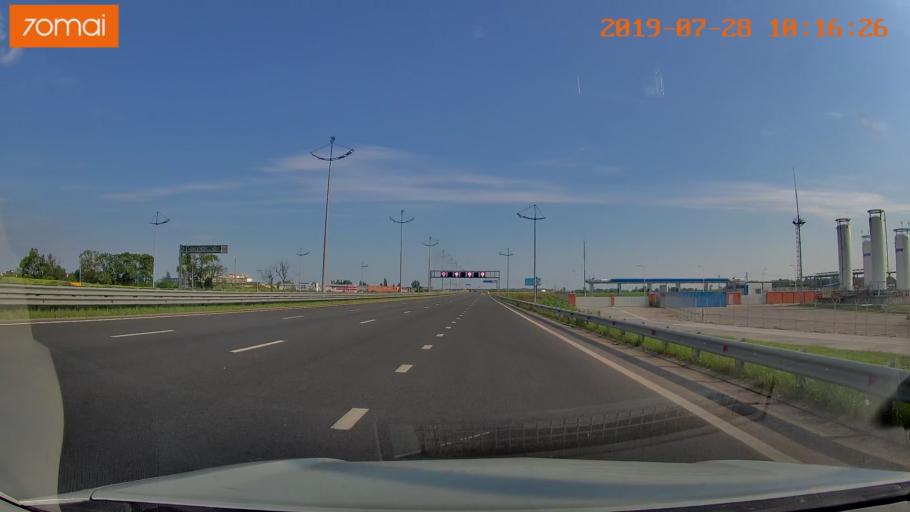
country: RU
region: Kaliningrad
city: Bol'shoe Isakovo
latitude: 54.7267
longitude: 20.5975
